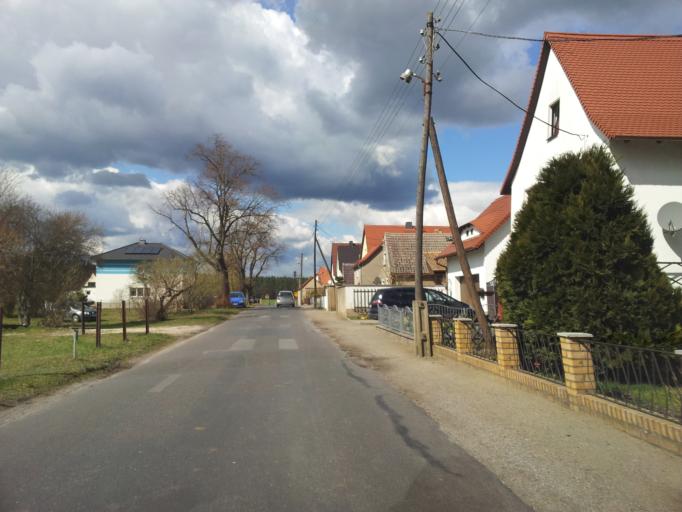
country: DE
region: Saxony
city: Rackelwitz
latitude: 51.3032
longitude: 14.2134
